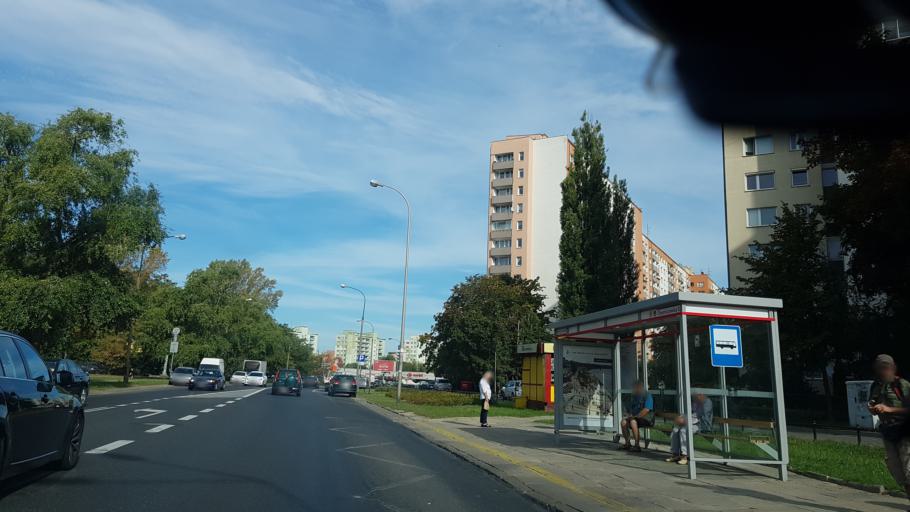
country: PL
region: Masovian Voivodeship
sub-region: Warszawa
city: Bielany
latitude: 52.2733
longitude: 20.9248
